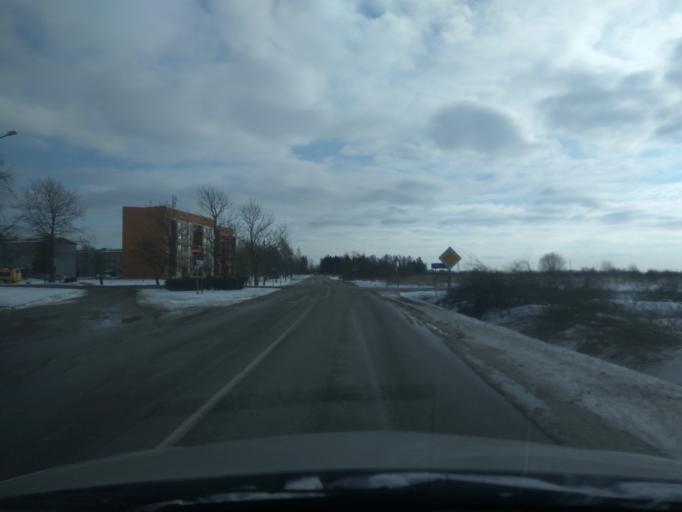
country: LV
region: Ventspils
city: Ventspils
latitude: 57.3332
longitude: 21.6346
